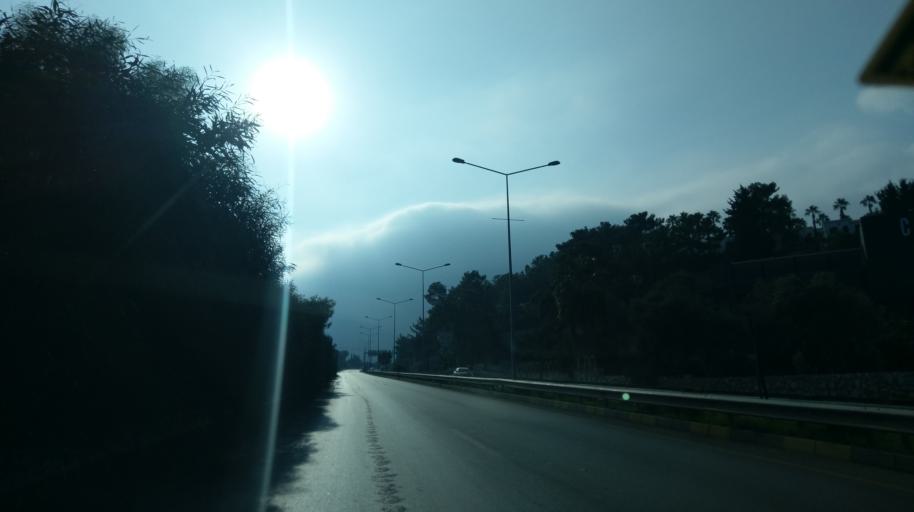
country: CY
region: Keryneia
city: Kyrenia
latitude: 35.3223
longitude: 33.3192
